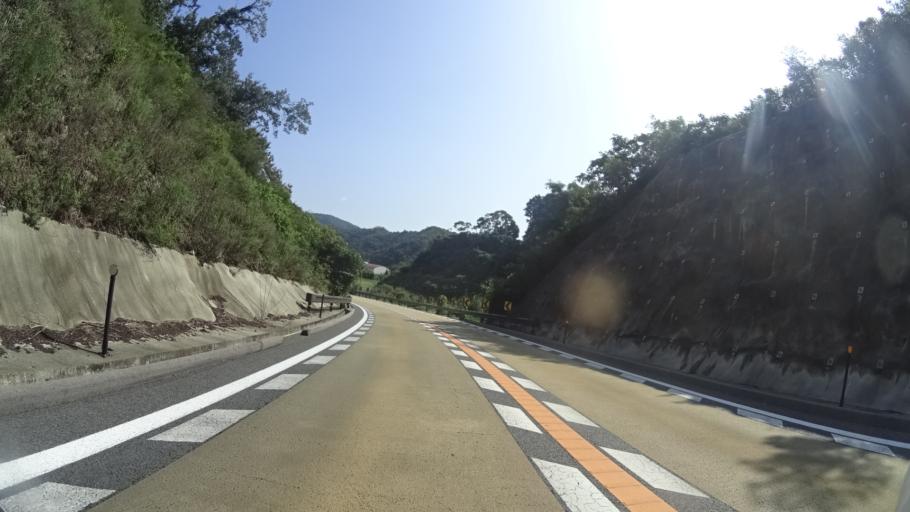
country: JP
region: Shimane
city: Gotsucho
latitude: 35.0694
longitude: 132.3309
